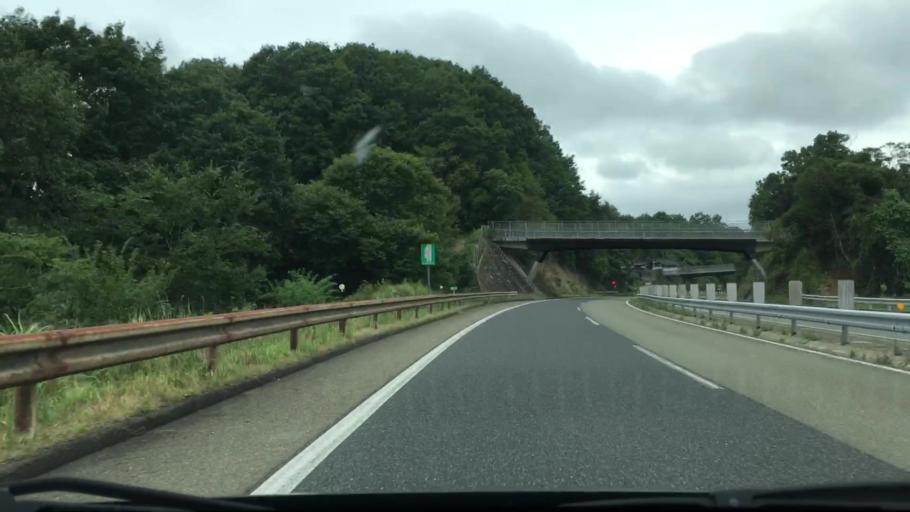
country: JP
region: Hiroshima
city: Shobara
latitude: 34.8284
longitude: 133.0500
